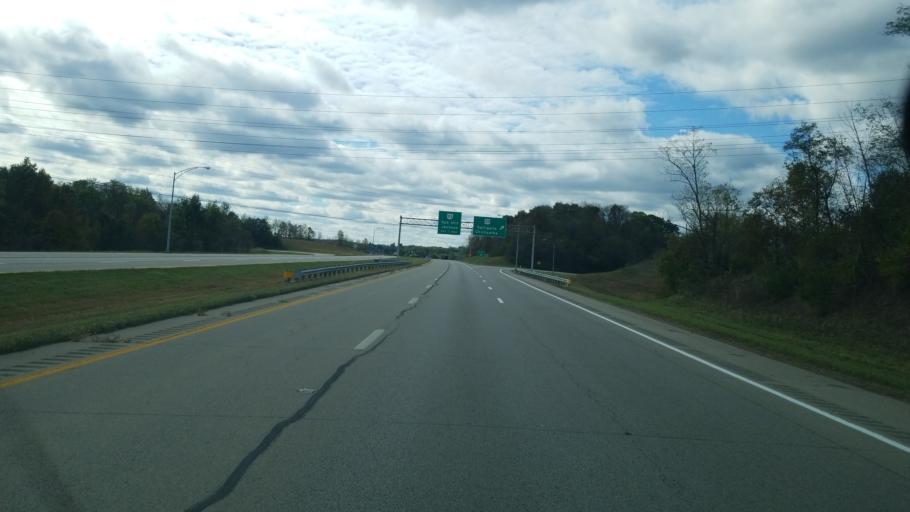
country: US
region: Ohio
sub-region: Jackson County
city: Jackson
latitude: 39.0483
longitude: -82.6062
